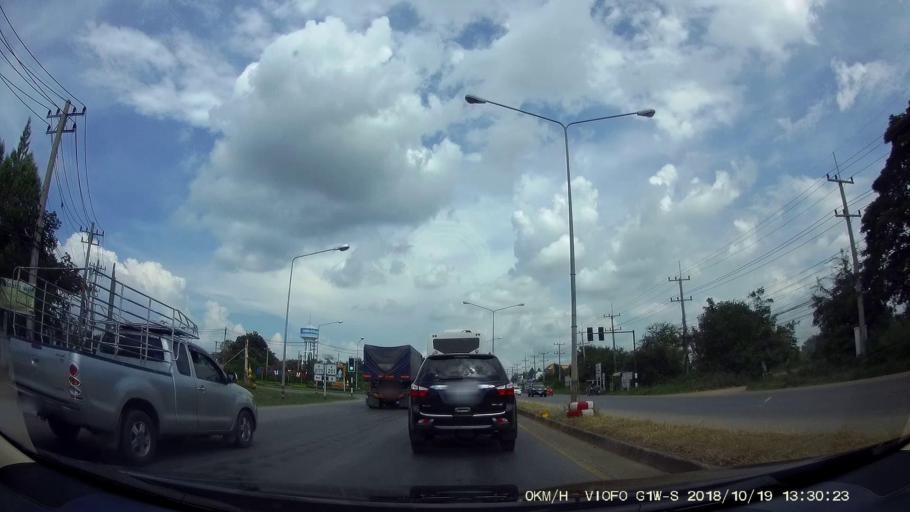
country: TH
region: Chaiyaphum
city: Chatturat
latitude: 15.5739
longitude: 101.8605
